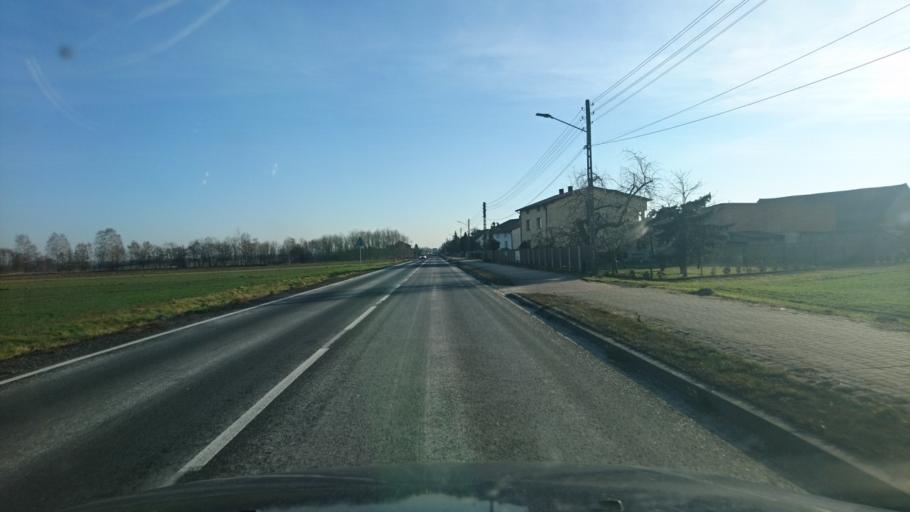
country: PL
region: Silesian Voivodeship
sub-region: Powiat klobucki
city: Starokrzepice
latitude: 51.0047
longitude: 18.6605
